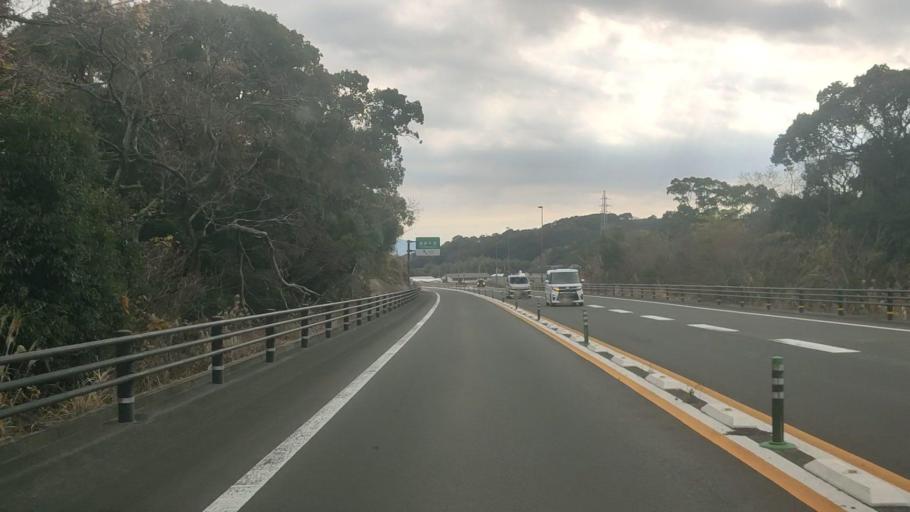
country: JP
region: Nagasaki
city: Shimabara
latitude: 32.7650
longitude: 130.3608
